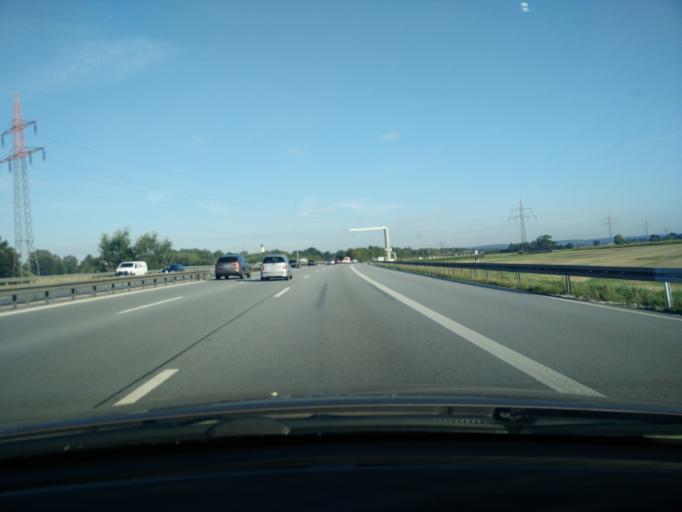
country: DE
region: Bavaria
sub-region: Upper Bavaria
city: Kranzberg
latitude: 48.3968
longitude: 11.5929
